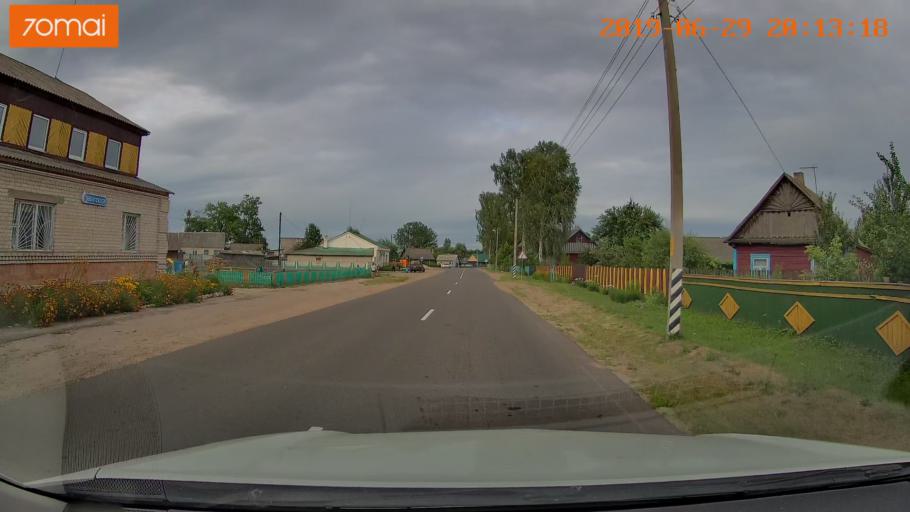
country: BY
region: Brest
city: Lahishyn
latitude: 52.3657
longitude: 26.1447
